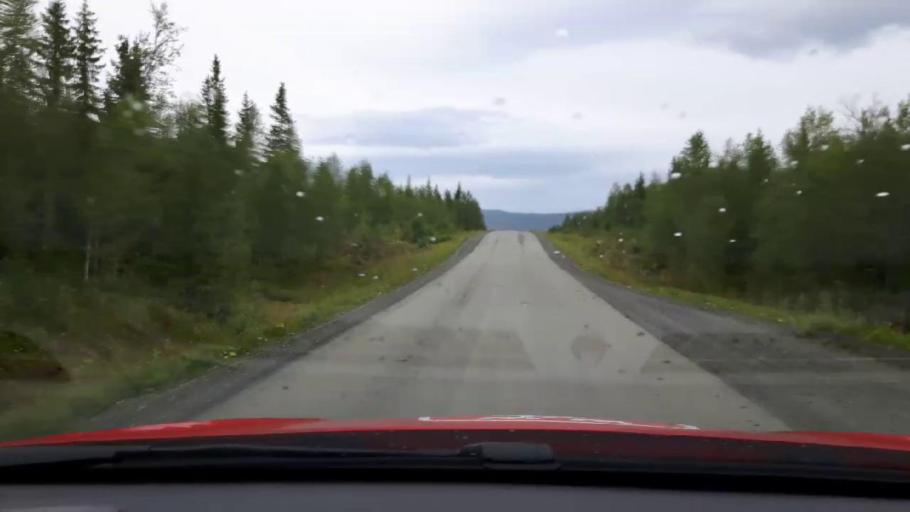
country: SE
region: Jaemtland
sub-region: Are Kommun
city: Are
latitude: 63.4300
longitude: 13.2145
